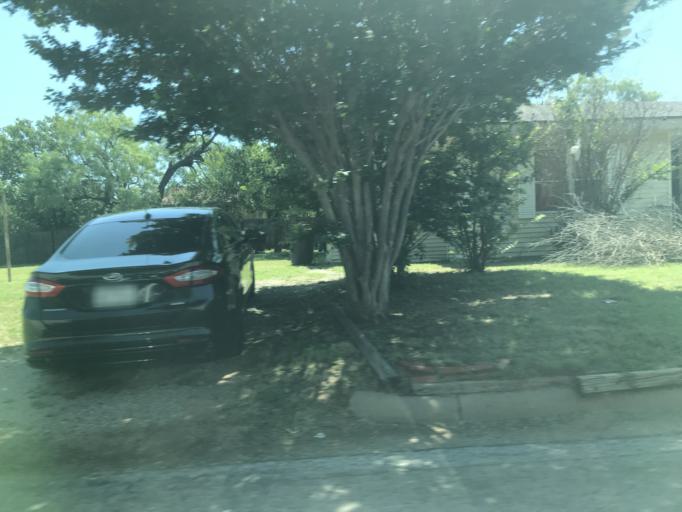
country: US
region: Texas
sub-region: Taylor County
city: Abilene
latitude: 32.4689
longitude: -99.7433
